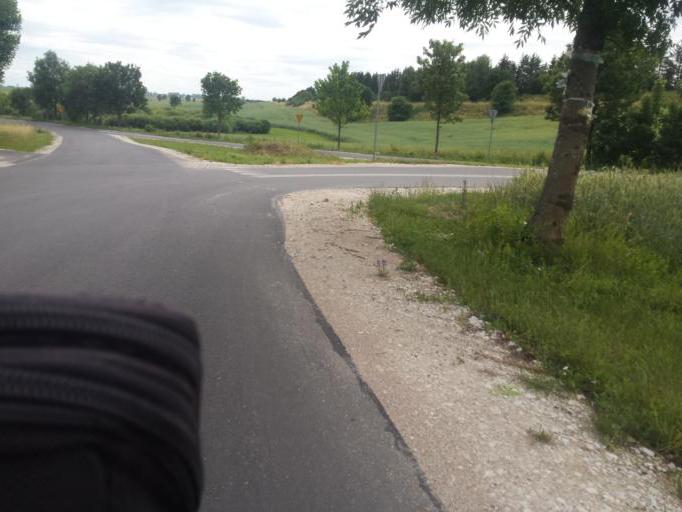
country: PL
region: Warmian-Masurian Voivodeship
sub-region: Powiat ilawski
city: Ilawa
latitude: 53.5186
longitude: 19.5543
